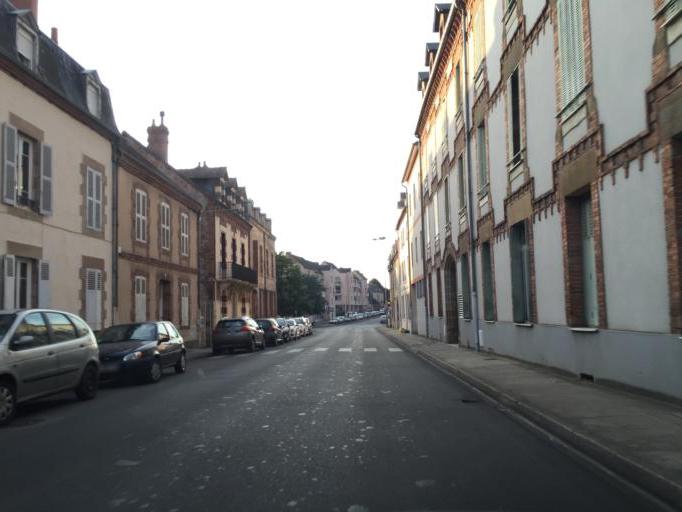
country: FR
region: Auvergne
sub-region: Departement de l'Allier
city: Moulins
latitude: 46.5656
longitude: 3.3392
